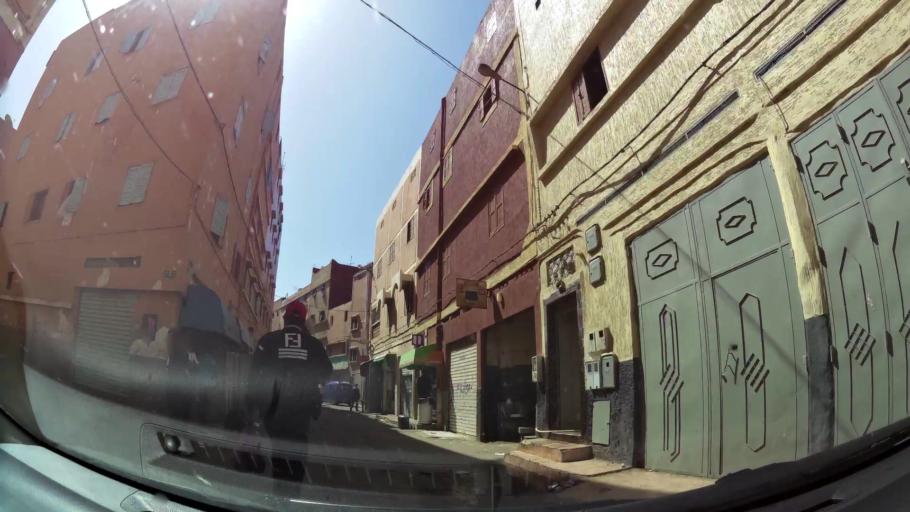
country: MA
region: Souss-Massa-Draa
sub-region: Inezgane-Ait Mellou
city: Inezgane
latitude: 30.3436
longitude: -9.5033
